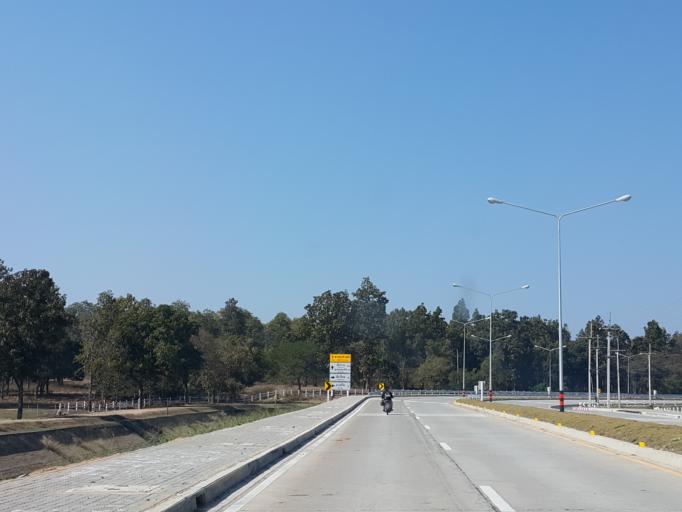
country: TH
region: Chiang Mai
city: Chiang Mai
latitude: 18.8639
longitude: 98.9594
